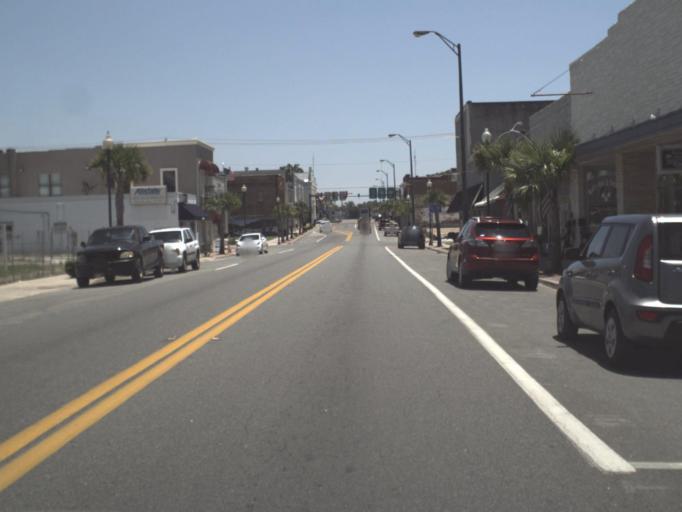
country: US
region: Florida
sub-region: Suwannee County
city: Live Oak
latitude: 30.2970
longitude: -82.9864
